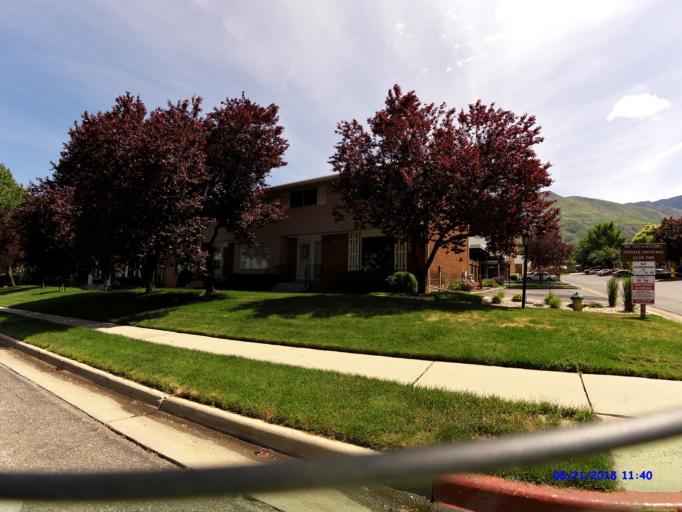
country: US
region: Utah
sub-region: Weber County
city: South Ogden
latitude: 41.1899
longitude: -111.9586
